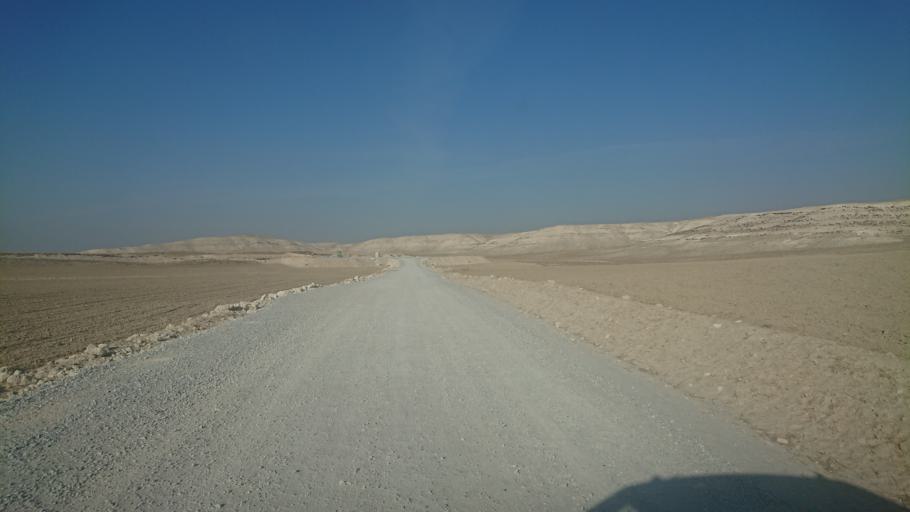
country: TR
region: Aksaray
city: Sultanhani
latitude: 38.0835
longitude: 33.6208
